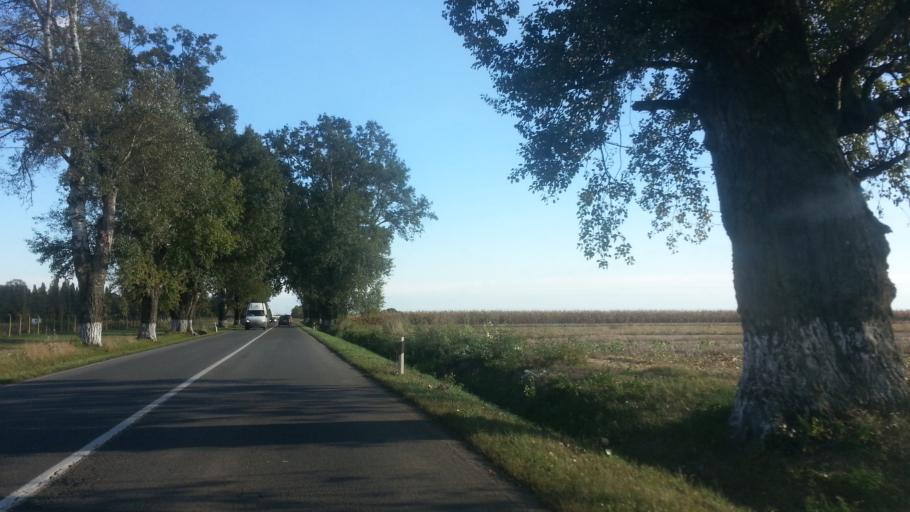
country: RS
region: Autonomna Pokrajina Vojvodina
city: Nova Pazova
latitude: 44.9253
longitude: 20.2468
